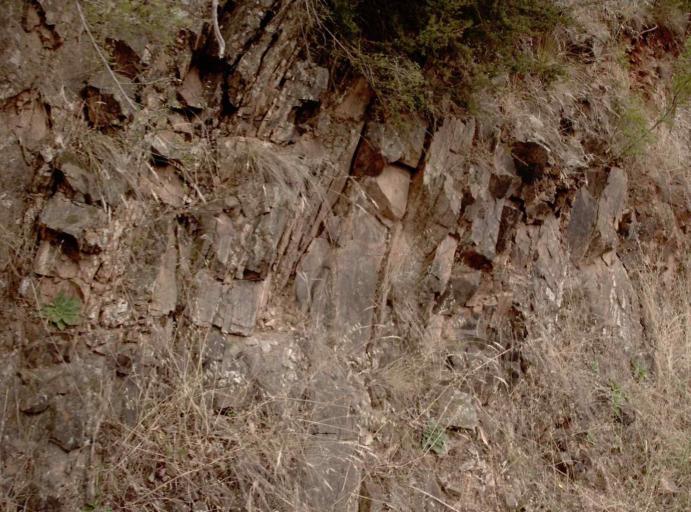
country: AU
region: Victoria
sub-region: Wellington
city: Heyfield
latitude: -37.6913
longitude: 146.6524
